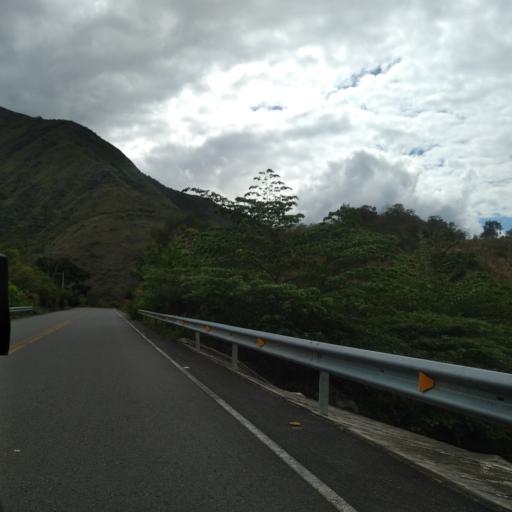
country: PE
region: Cajamarca
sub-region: Provincia de San Ignacio
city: Chirinos
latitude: -5.2359
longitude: -78.8611
